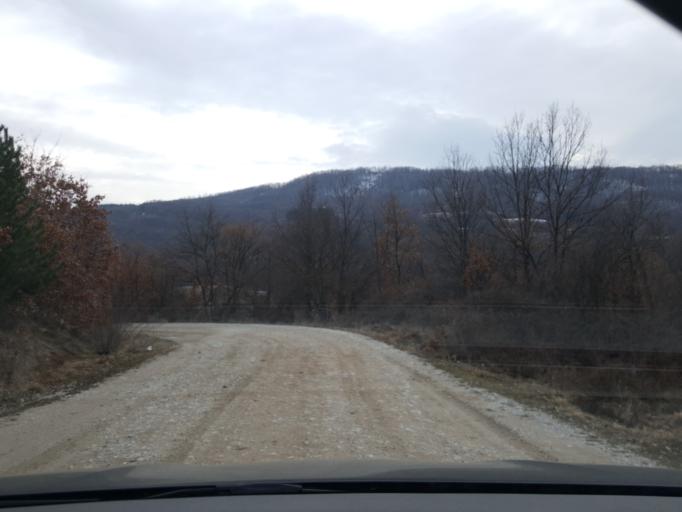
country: RS
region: Central Serbia
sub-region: Pirotski Okrug
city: Dimitrovgrad
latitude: 42.9990
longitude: 22.7469
